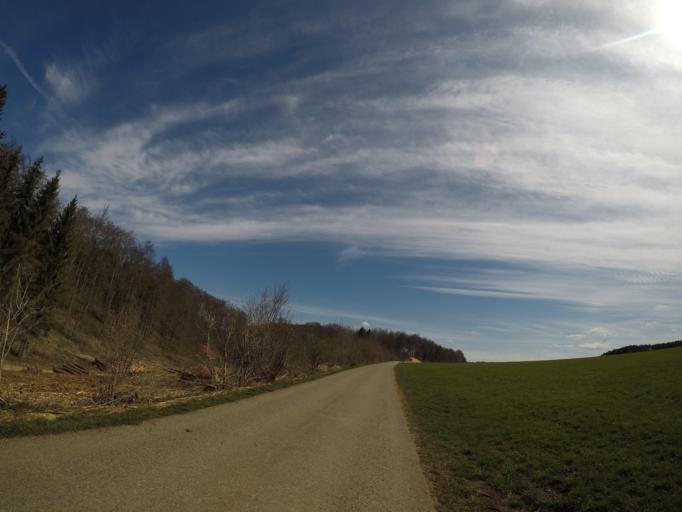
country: DE
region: Baden-Wuerttemberg
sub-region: Tuebingen Region
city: Mehrstetten
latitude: 48.3462
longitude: 9.5761
